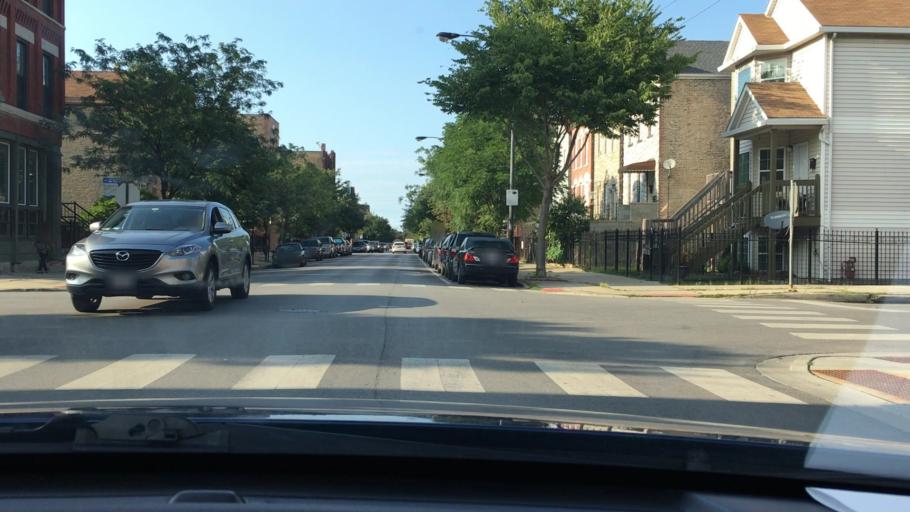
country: US
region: Illinois
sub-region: Cook County
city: Chicago
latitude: 41.8551
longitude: -87.6612
